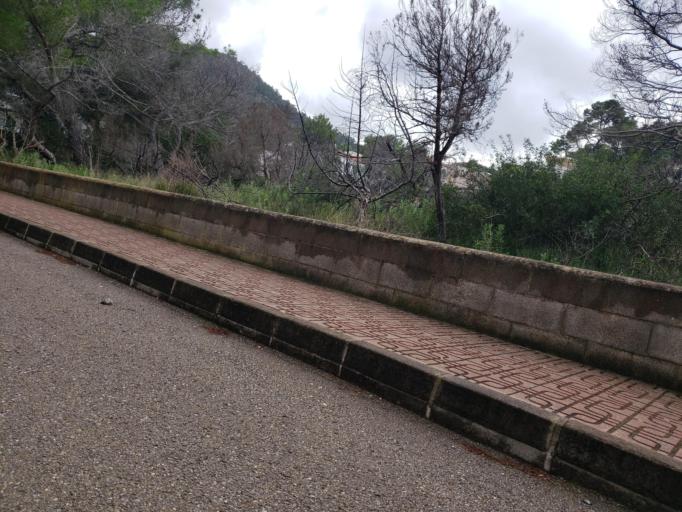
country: ES
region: Balearic Islands
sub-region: Illes Balears
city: Sant Joan de Labritja
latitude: 39.1092
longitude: 1.5135
